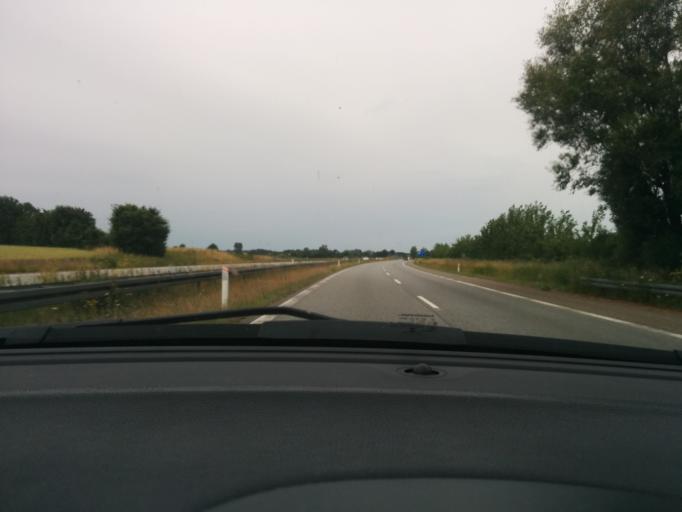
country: DK
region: Zealand
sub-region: Faxe Kommune
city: Ronnede
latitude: 55.3483
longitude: 12.0630
